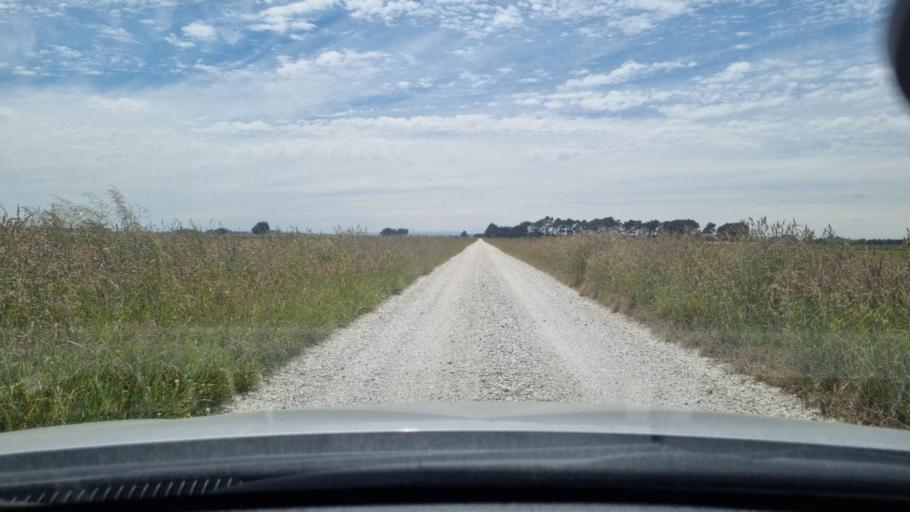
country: NZ
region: Southland
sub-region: Invercargill City
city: Invercargill
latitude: -46.3799
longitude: 168.2702
